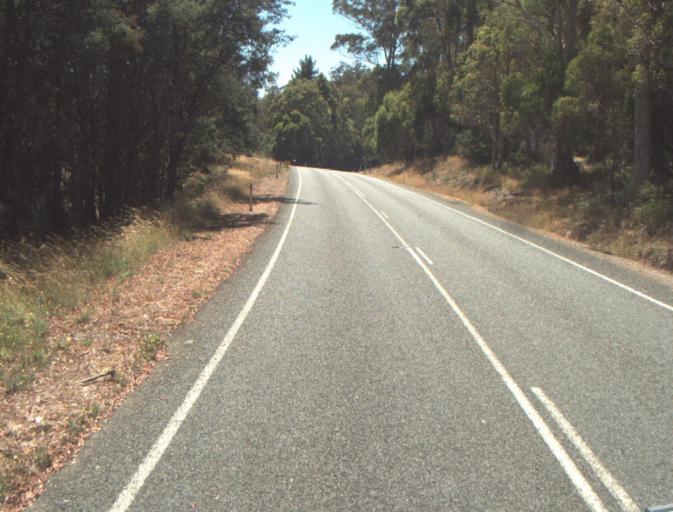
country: AU
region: Tasmania
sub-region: Dorset
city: Scottsdale
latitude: -41.3166
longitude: 147.3665
